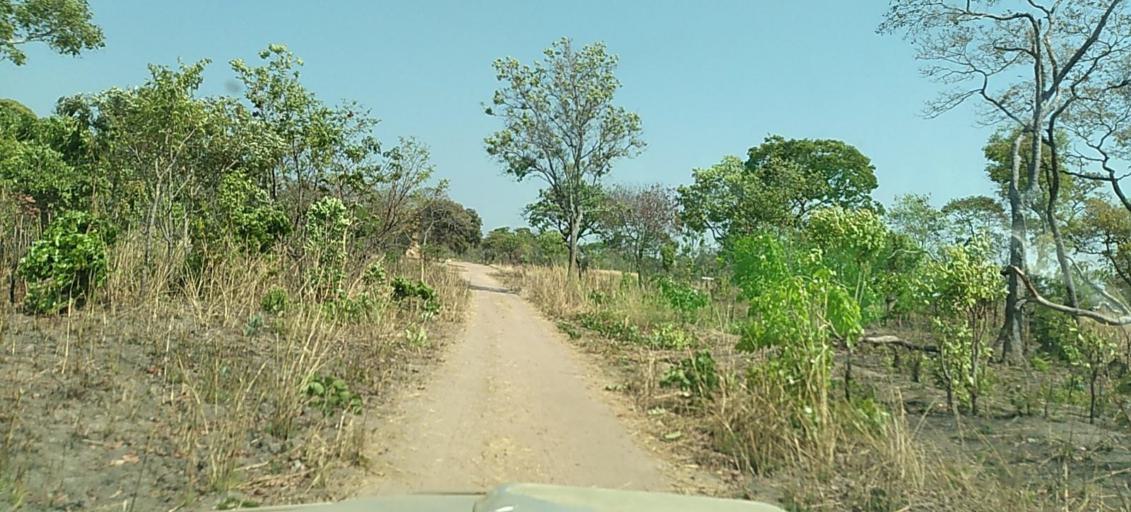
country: ZM
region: North-Western
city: Kalengwa
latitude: -13.3088
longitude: 24.8079
